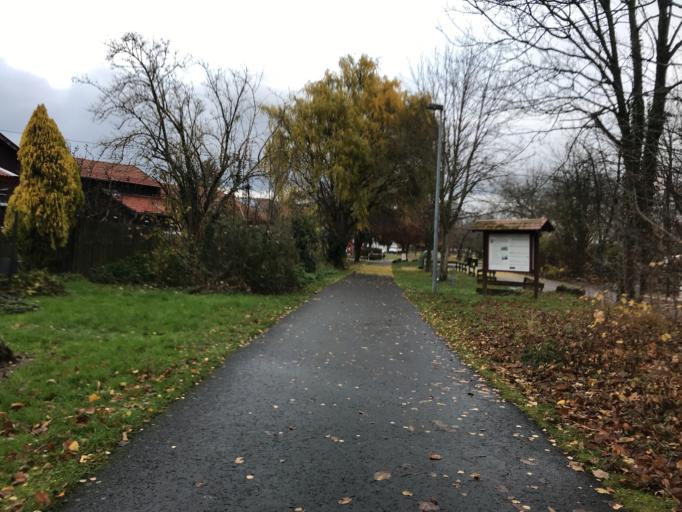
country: DE
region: Rheinland-Pfalz
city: Gau-Bischofsheim
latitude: 49.9131
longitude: 8.2782
